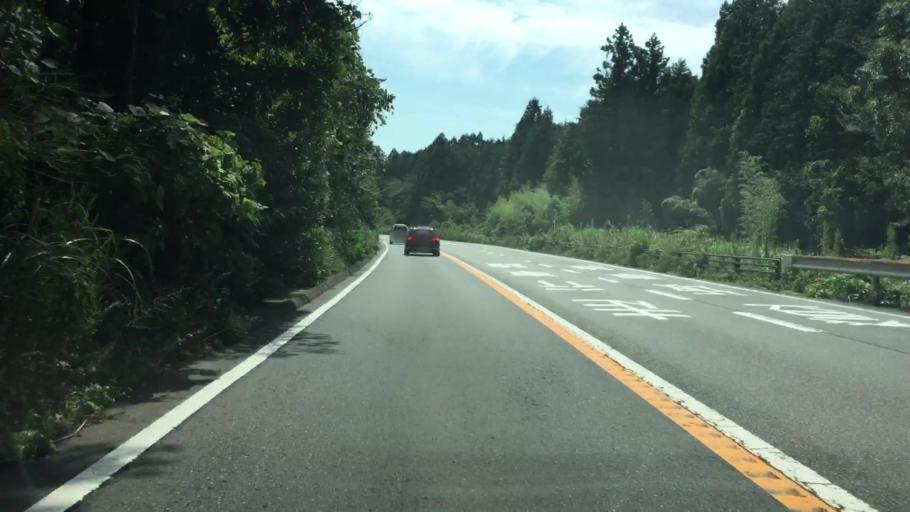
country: JP
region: Shizuoka
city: Fujinomiya
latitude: 35.3007
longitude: 138.6034
